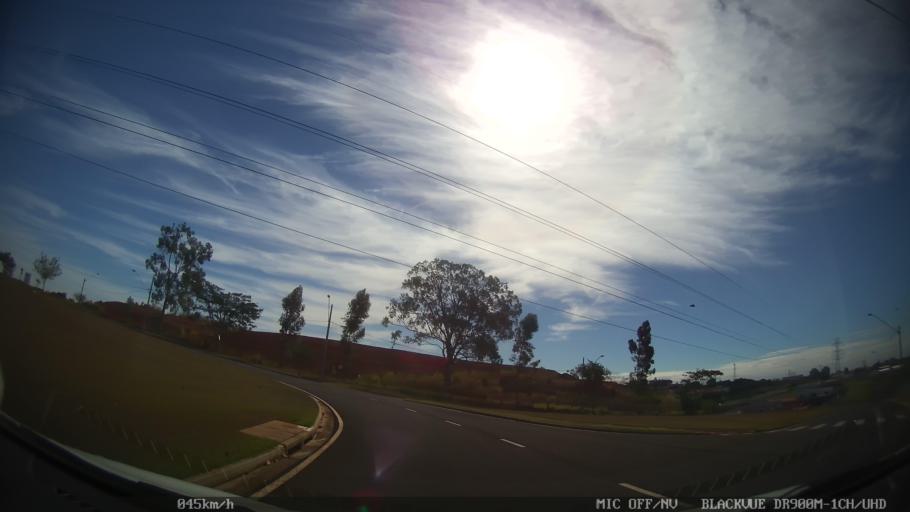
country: BR
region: Sao Paulo
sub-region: Sao Jose Do Rio Preto
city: Sao Jose do Rio Preto
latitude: -20.8508
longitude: -49.3752
